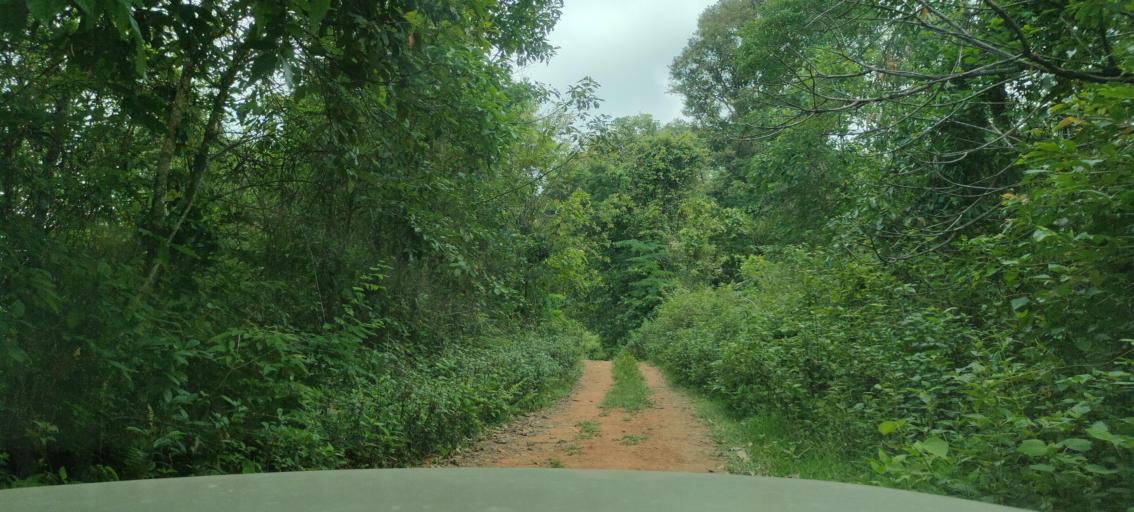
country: LA
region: Loungnamtha
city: Muang Nale
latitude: 20.4238
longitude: 101.4667
